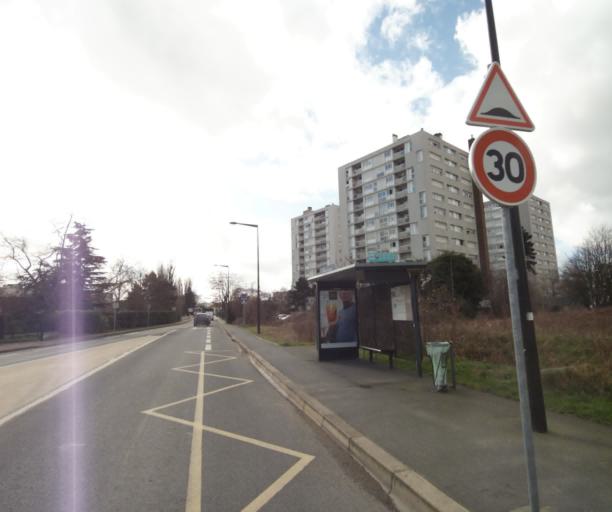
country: FR
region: Ile-de-France
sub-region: Departement de Seine-Saint-Denis
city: Villetaneuse
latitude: 48.9547
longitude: 2.3386
